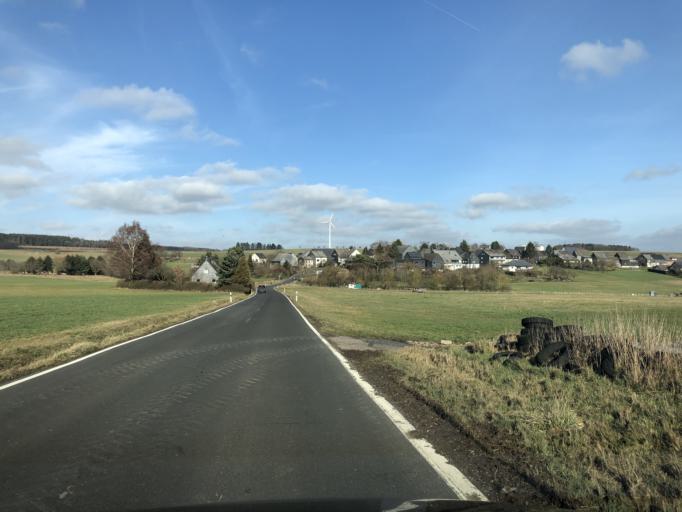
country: DE
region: Rheinland-Pfalz
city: Wahlenau
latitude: 49.9008
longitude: 7.2466
